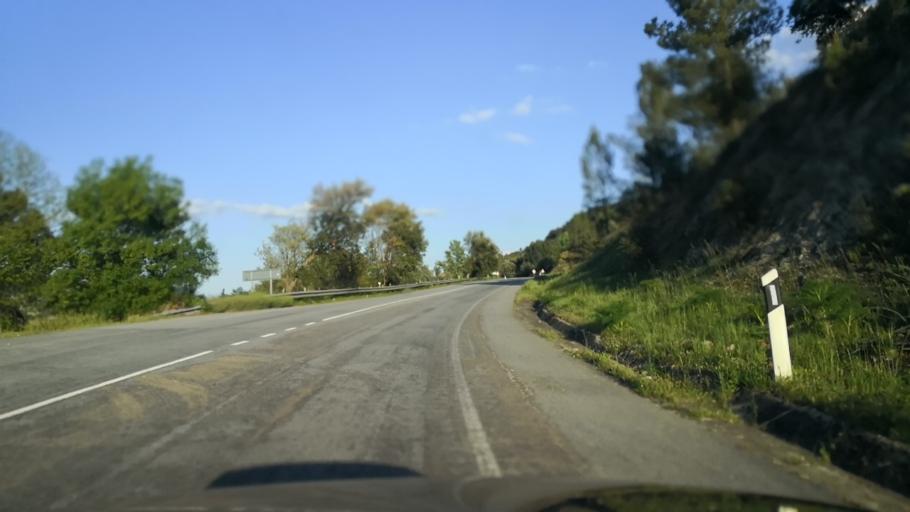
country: PT
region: Portalegre
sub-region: Marvao
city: Marvao
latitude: 39.3818
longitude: -7.3790
